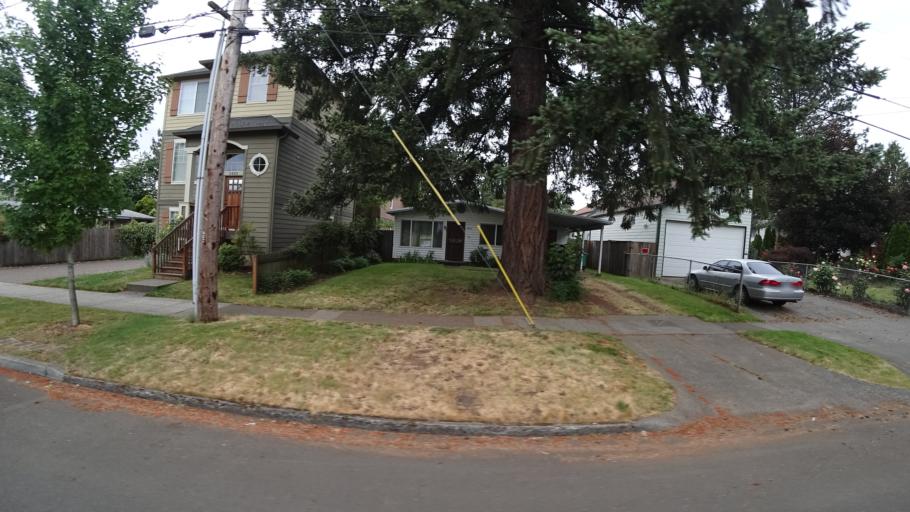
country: US
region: Oregon
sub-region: Multnomah County
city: Lents
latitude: 45.4835
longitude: -122.5709
